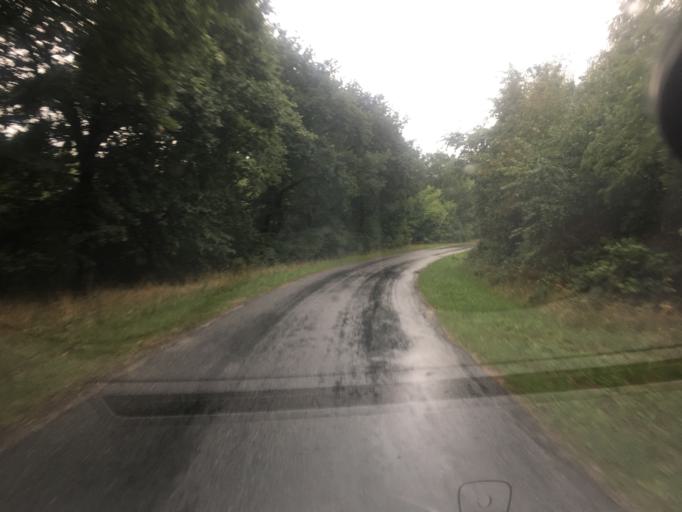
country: DK
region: South Denmark
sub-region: Tonder Kommune
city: Logumkloster
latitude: 55.0428
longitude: 8.9399
